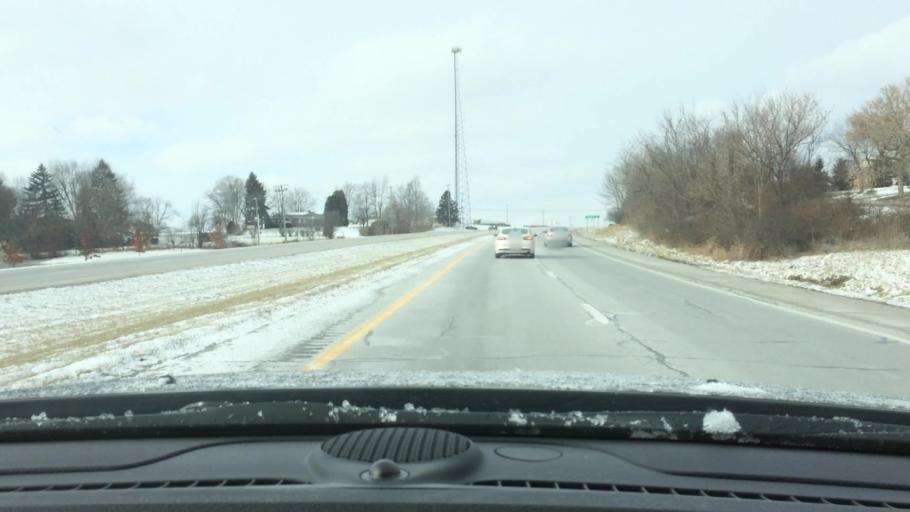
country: US
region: Ohio
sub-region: Wayne County
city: Dalton
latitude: 40.7952
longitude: -81.7035
